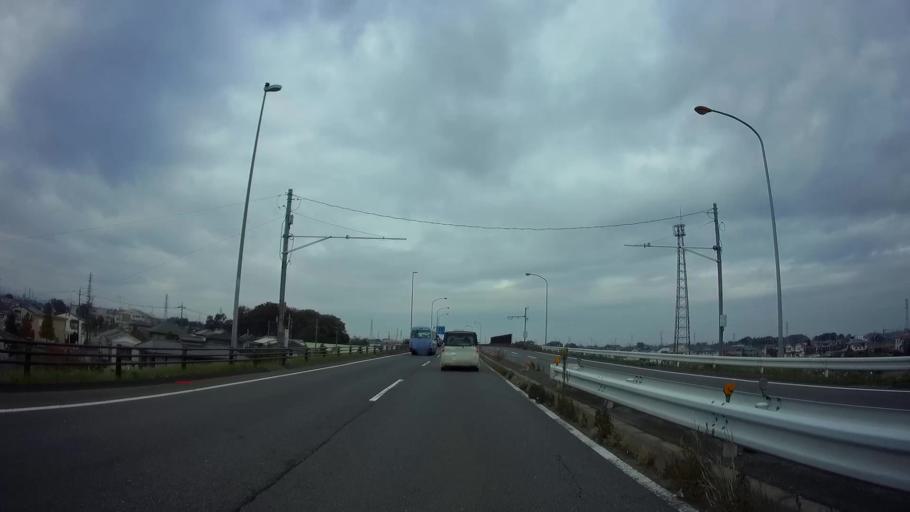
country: JP
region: Saitama
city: Kumagaya
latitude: 36.1694
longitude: 139.3777
